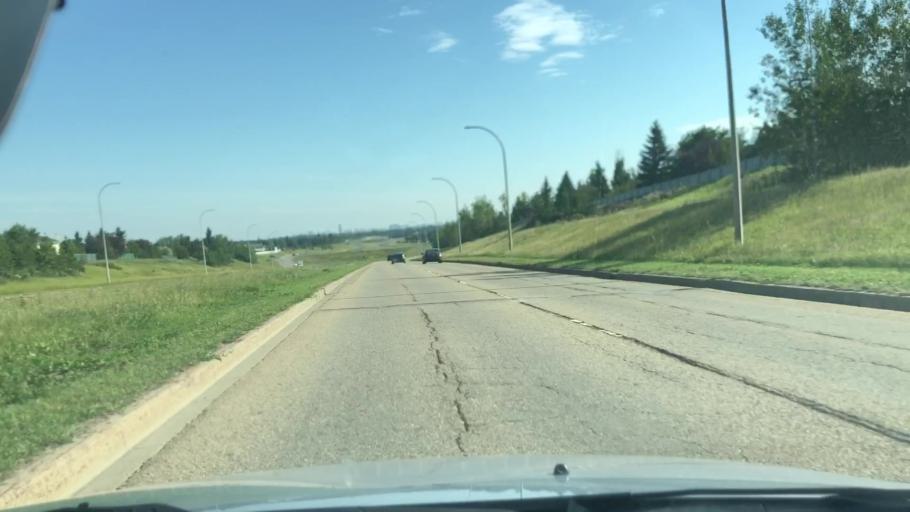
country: CA
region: Alberta
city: Edmonton
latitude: 53.4631
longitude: -113.5858
